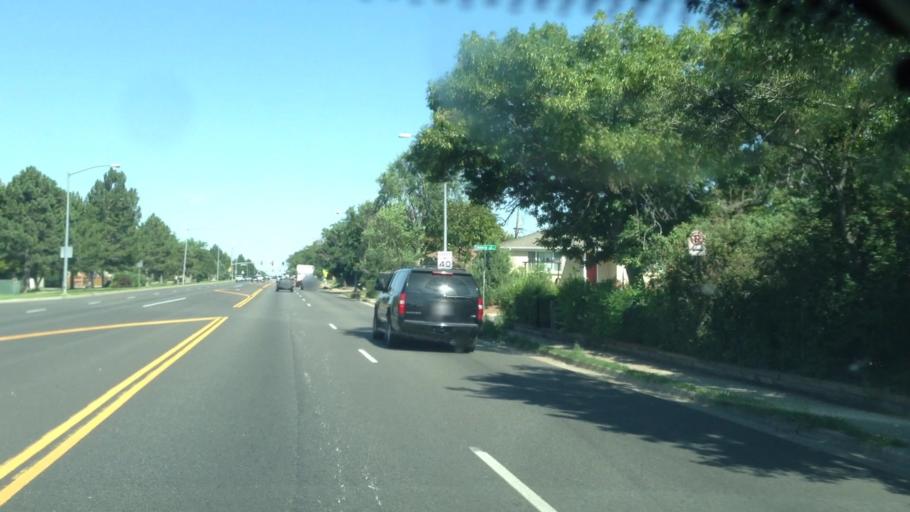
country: US
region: Colorado
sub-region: Adams County
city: Aurora
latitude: 39.7255
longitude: -104.8749
